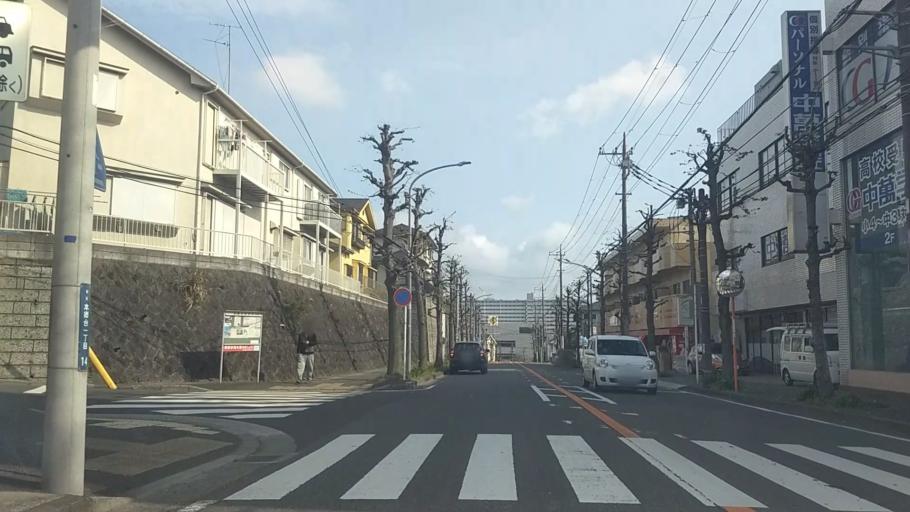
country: JP
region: Kanagawa
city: Kamakura
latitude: 35.3712
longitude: 139.5467
